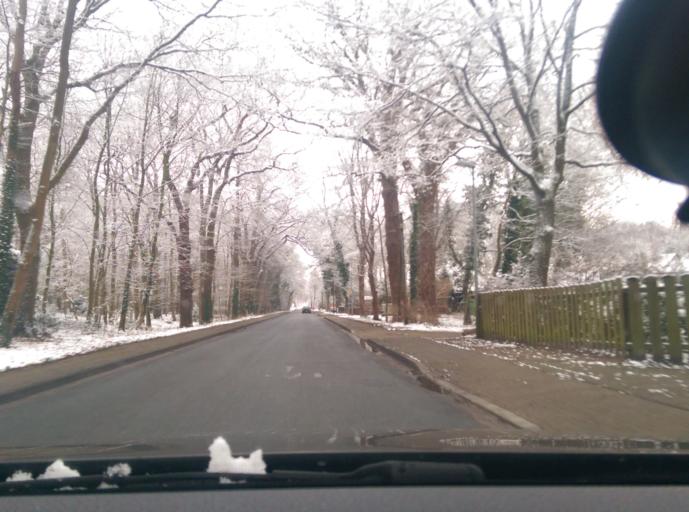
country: DE
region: Lower Saxony
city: Schwarmstedt
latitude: 52.6736
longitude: 9.6229
